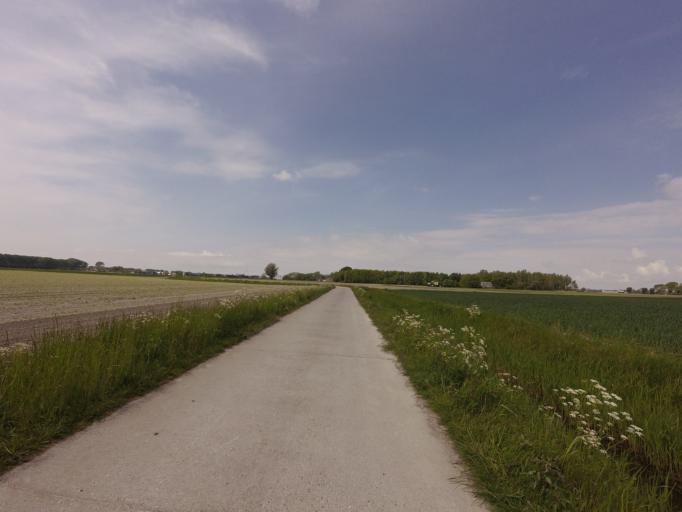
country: NL
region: Friesland
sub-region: Sudwest Fryslan
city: Bolsward
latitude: 53.1073
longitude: 5.4857
